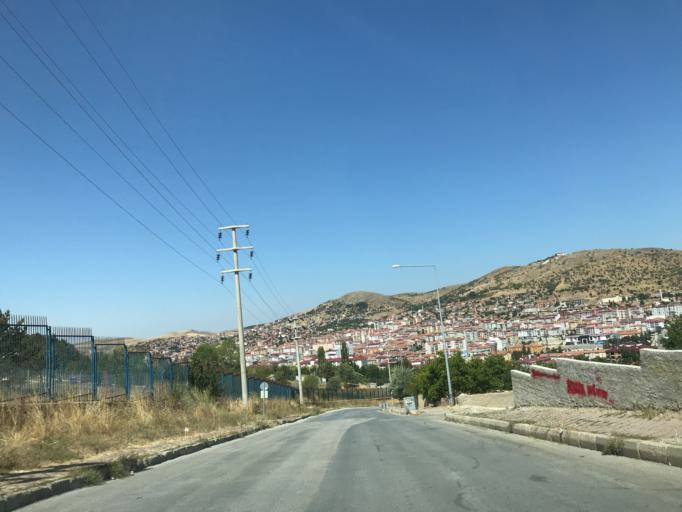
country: TR
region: Yozgat
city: Yozgat
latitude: 39.8167
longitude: 34.8205
